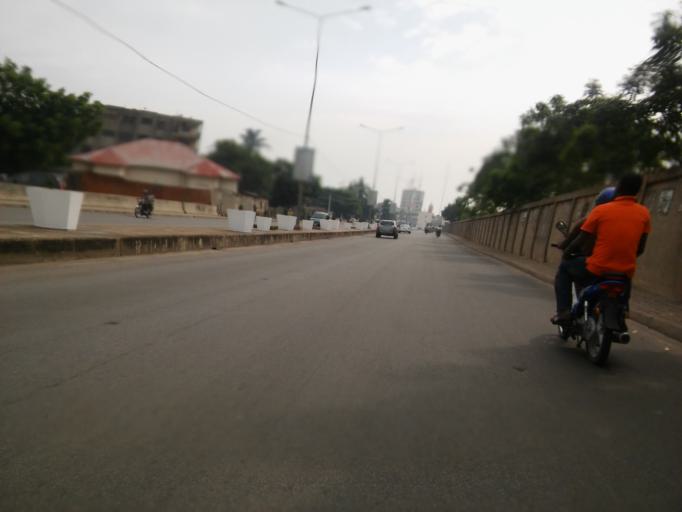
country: BJ
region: Littoral
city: Cotonou
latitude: 6.3562
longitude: 2.4328
